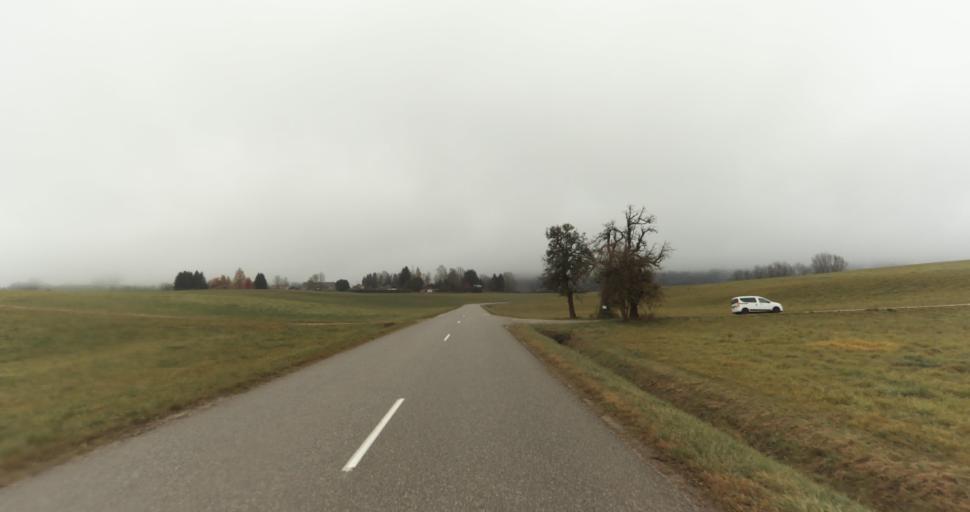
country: FR
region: Rhone-Alpes
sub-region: Departement de la Haute-Savoie
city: Etaux
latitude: 46.0276
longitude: 6.2844
